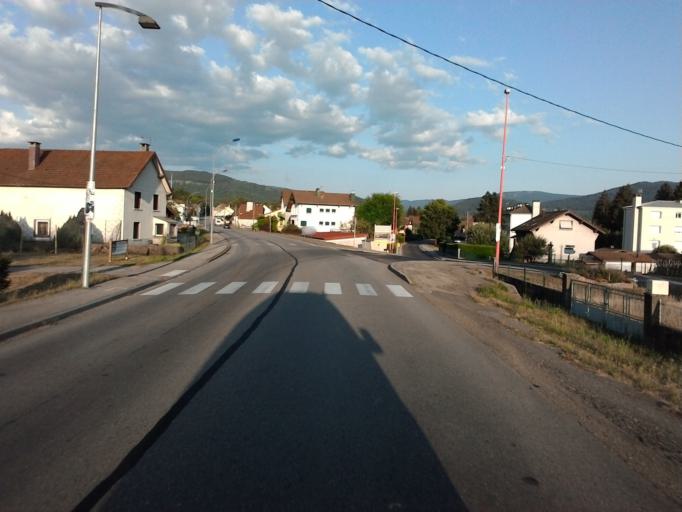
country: FR
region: Lorraine
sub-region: Departement des Vosges
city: Ramonchamp
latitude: 47.8949
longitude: 6.7350
